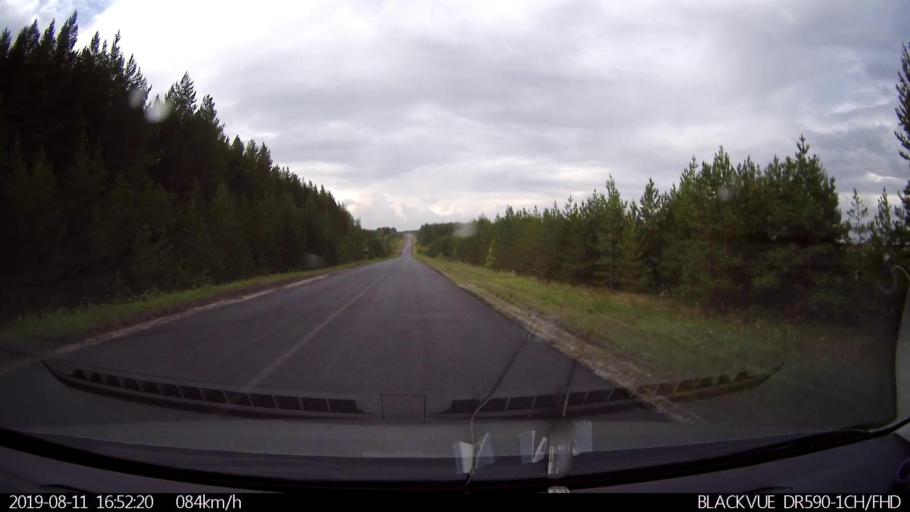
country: RU
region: Ulyanovsk
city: Mayna
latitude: 54.2469
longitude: 47.6745
